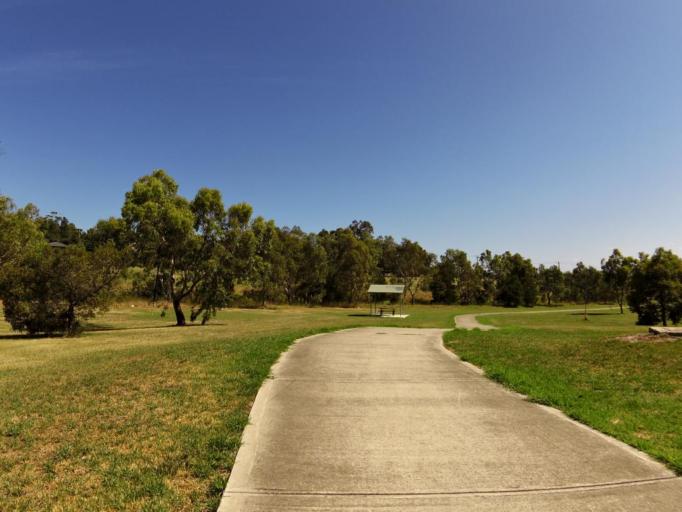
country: AU
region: Victoria
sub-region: Hume
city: Broadmeadows
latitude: -37.6750
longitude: 144.9113
